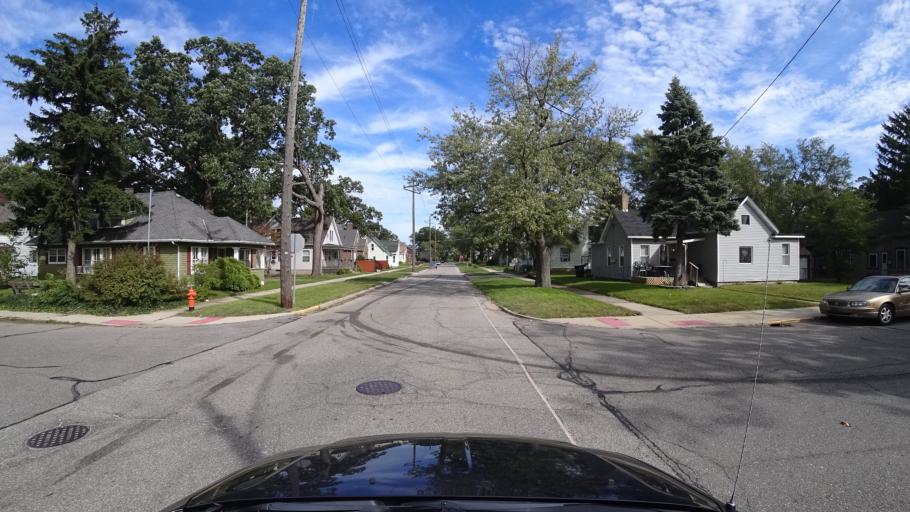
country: US
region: Indiana
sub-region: LaPorte County
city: Michigan City
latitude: 41.7141
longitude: -86.8863
